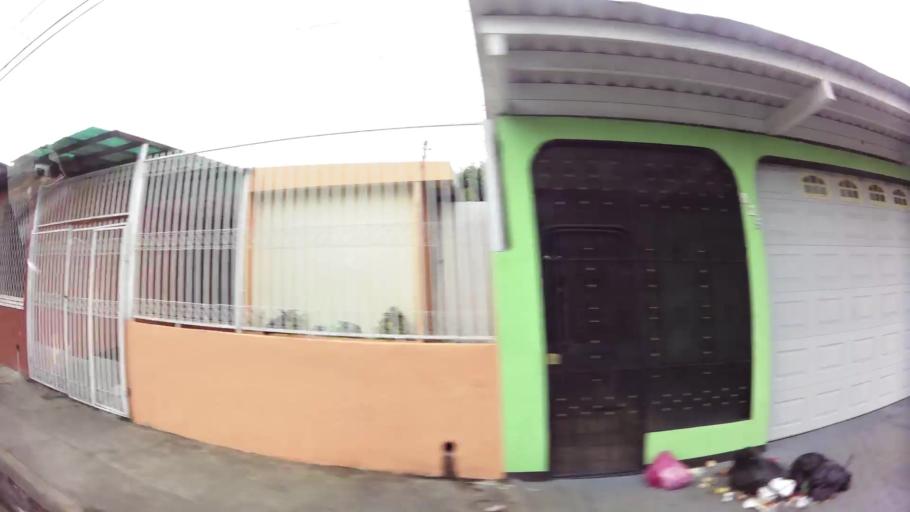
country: NI
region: Managua
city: Managua
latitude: 12.1267
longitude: -86.2279
